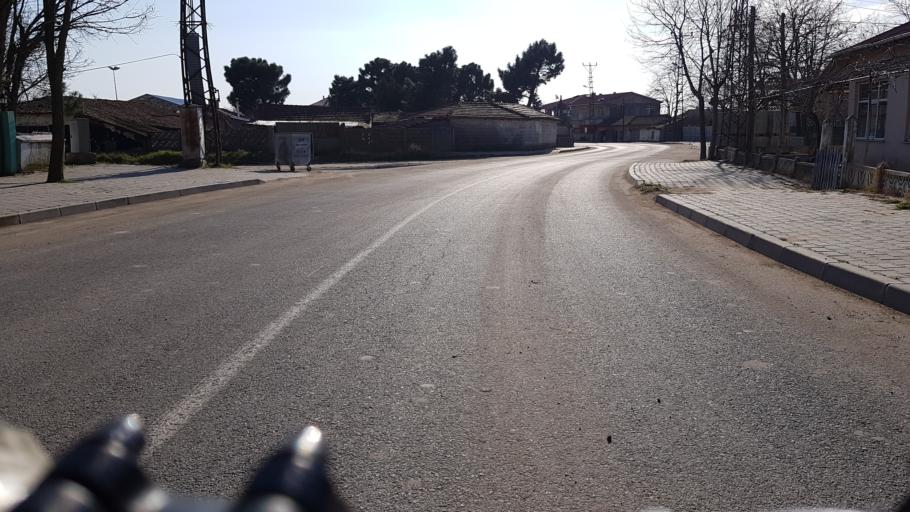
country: TR
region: Tekirdag
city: Velimese
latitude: 41.3451
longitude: 27.8356
